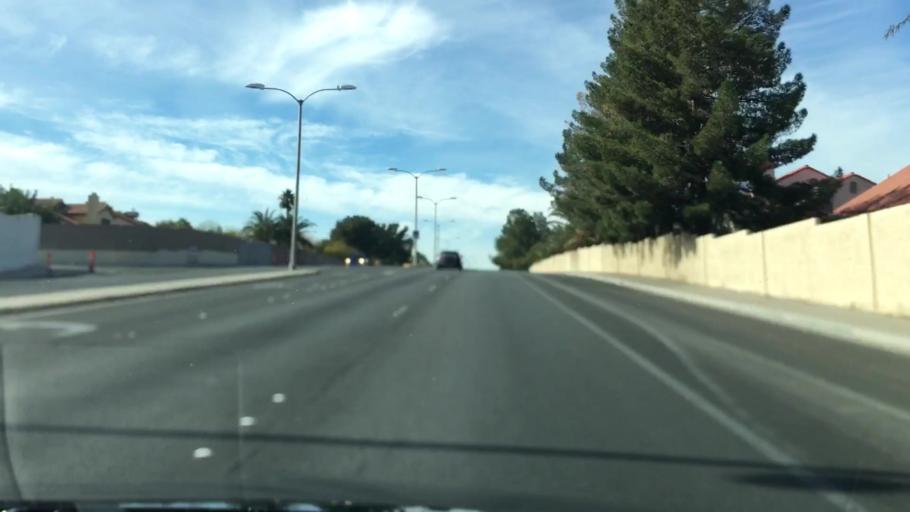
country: US
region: Nevada
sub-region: Clark County
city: Whitney
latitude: 36.0563
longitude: -115.0618
